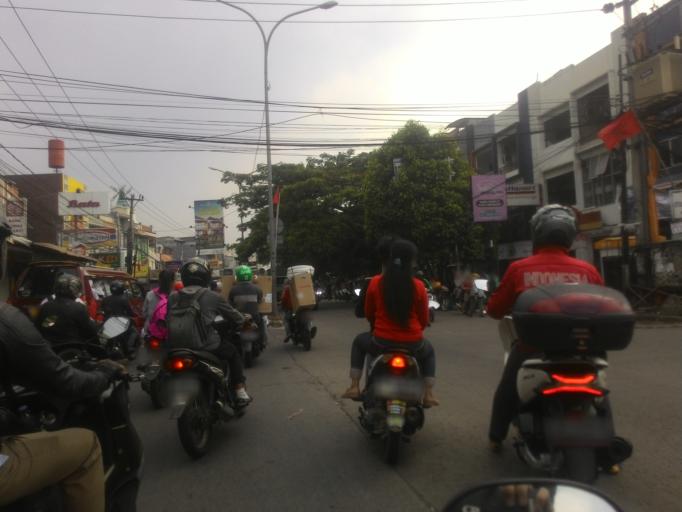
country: ID
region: West Java
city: Depok
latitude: -6.4054
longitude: 106.8190
